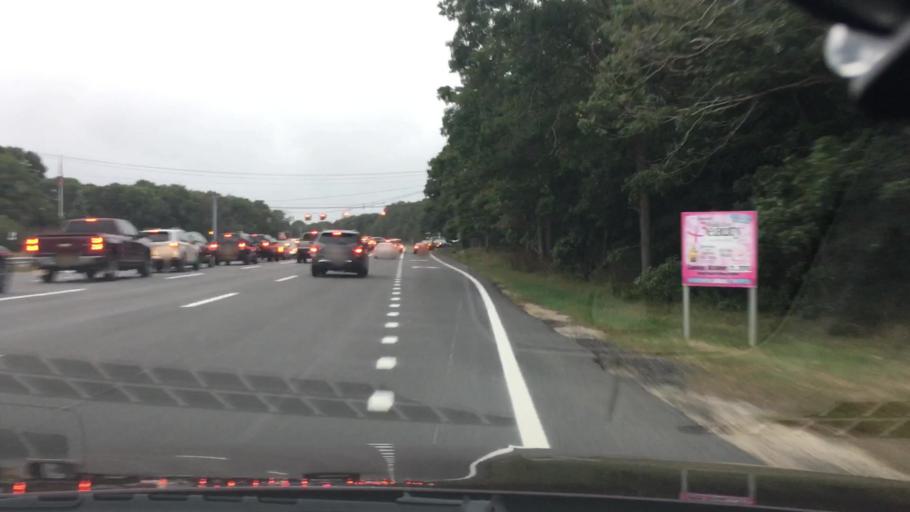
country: US
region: New York
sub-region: Suffolk County
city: Centereach
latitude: 40.8843
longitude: -73.1078
